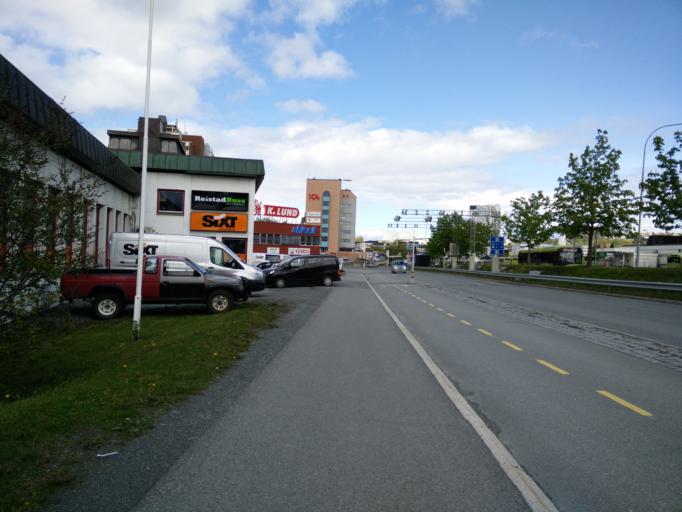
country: NO
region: Sor-Trondelag
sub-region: Trondheim
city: Trondheim
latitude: 63.4057
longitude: 10.3967
